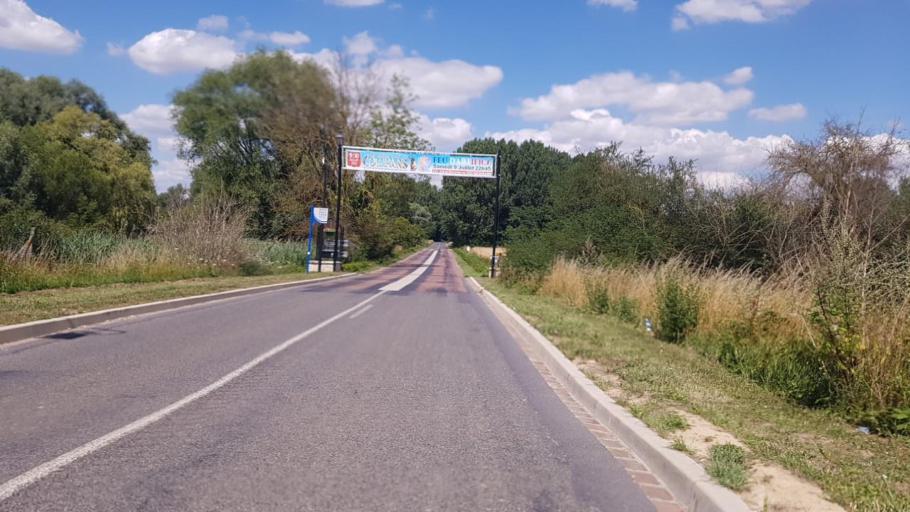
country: FR
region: Ile-de-France
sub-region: Departement de Seine-et-Marne
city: Juilly
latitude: 48.9965
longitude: 2.6652
